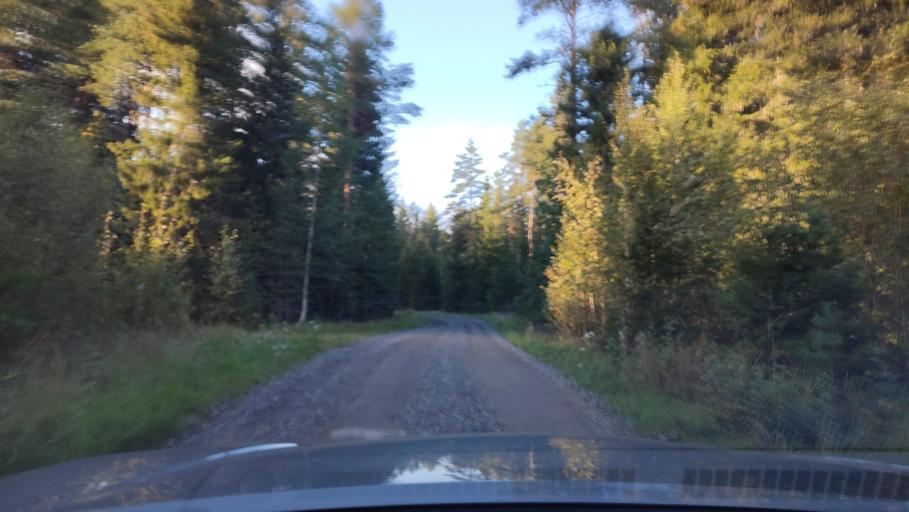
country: FI
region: Southern Ostrobothnia
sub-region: Suupohja
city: Karijoki
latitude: 62.2150
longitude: 21.5727
